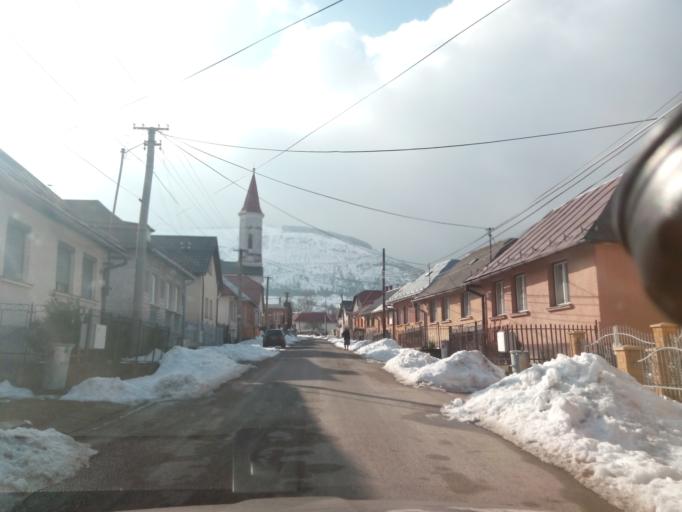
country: SK
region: Presovsky
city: Stara L'ubovna
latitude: 49.2250
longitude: 20.7498
